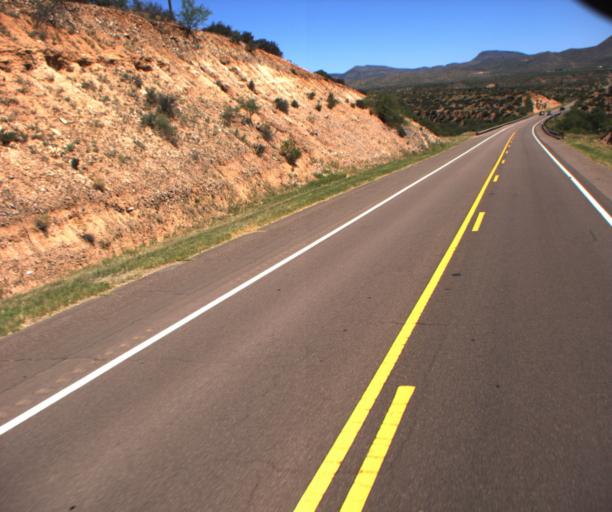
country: US
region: Arizona
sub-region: Gila County
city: Globe
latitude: 33.4080
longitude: -110.7425
